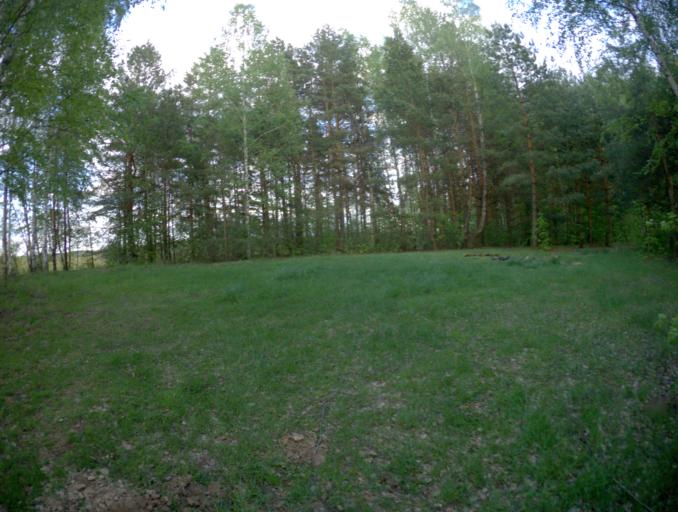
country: RU
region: Rjazan
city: Spas-Klepiki
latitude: 55.2554
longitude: 40.1136
